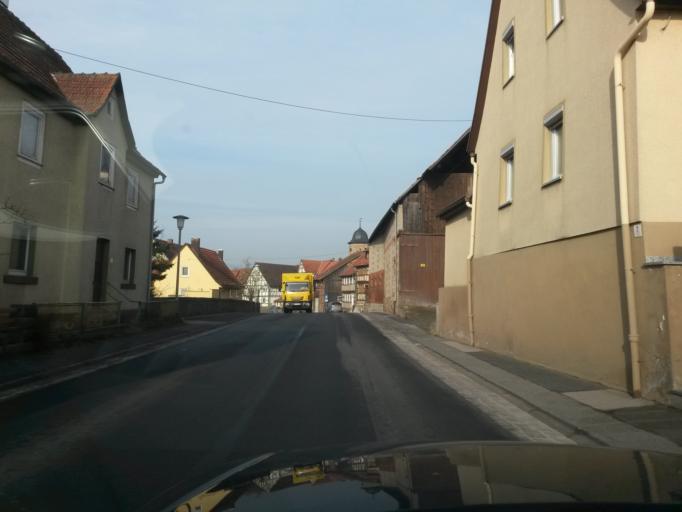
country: DE
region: Bavaria
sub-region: Regierungsbezirk Unterfranken
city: Sondheim vor der Rhoen
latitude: 50.4783
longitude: 10.1865
